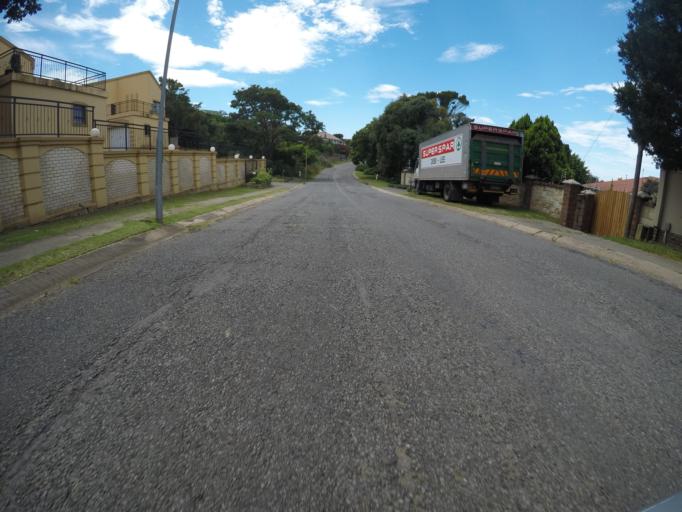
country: ZA
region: Eastern Cape
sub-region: Buffalo City Metropolitan Municipality
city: East London
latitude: -33.0372
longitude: 27.8599
